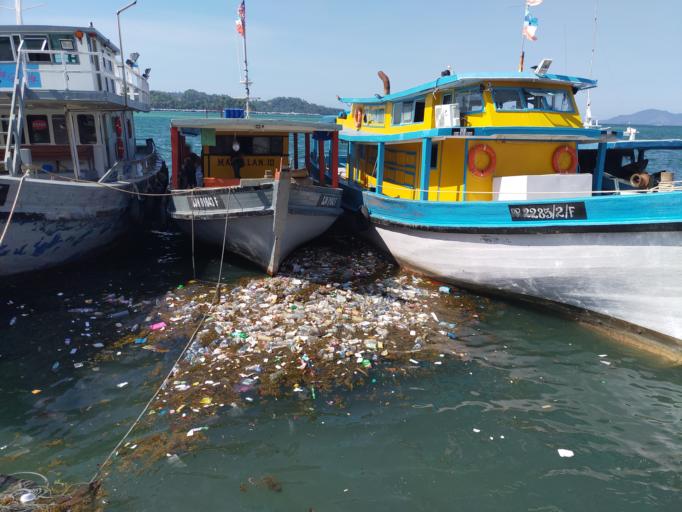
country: MY
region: Sabah
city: Kota Kinabalu
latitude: 5.9844
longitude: 116.0738
